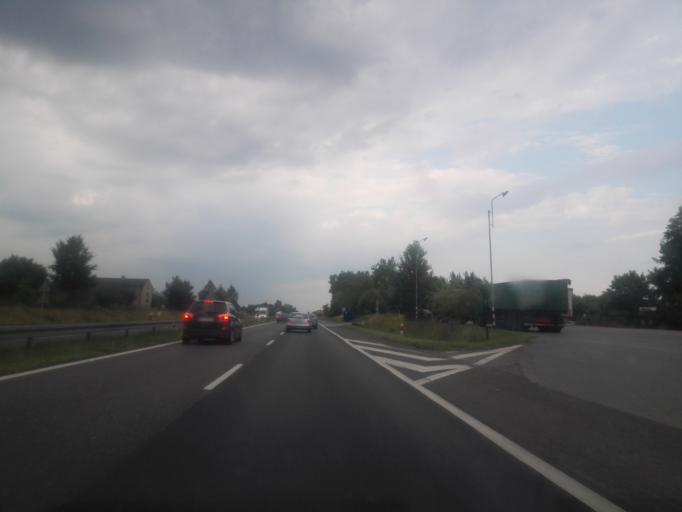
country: PL
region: Silesian Voivodeship
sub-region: Powiat czestochowski
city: Kamienica Polska
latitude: 50.6779
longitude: 19.1267
